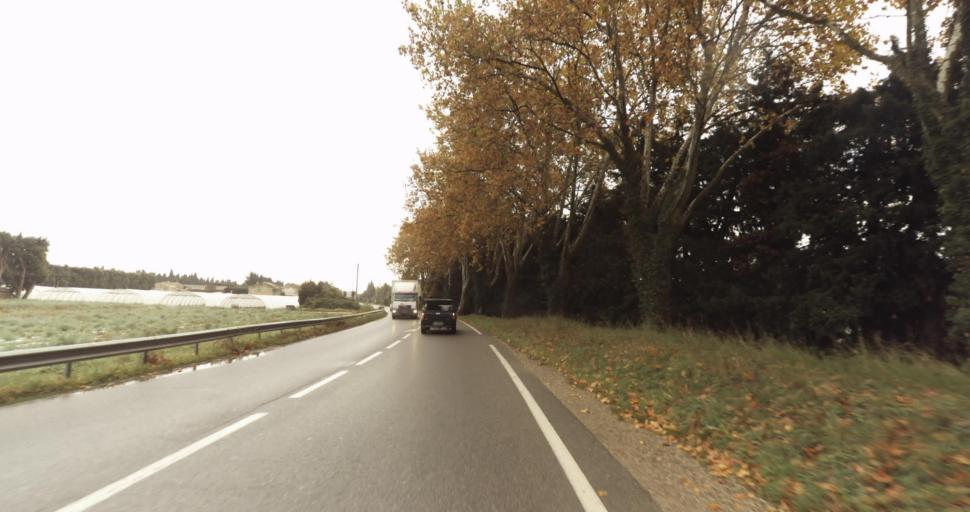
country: FR
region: Provence-Alpes-Cote d'Azur
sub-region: Departement des Bouches-du-Rhone
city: Rognonas
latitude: 43.8958
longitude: 4.7878
